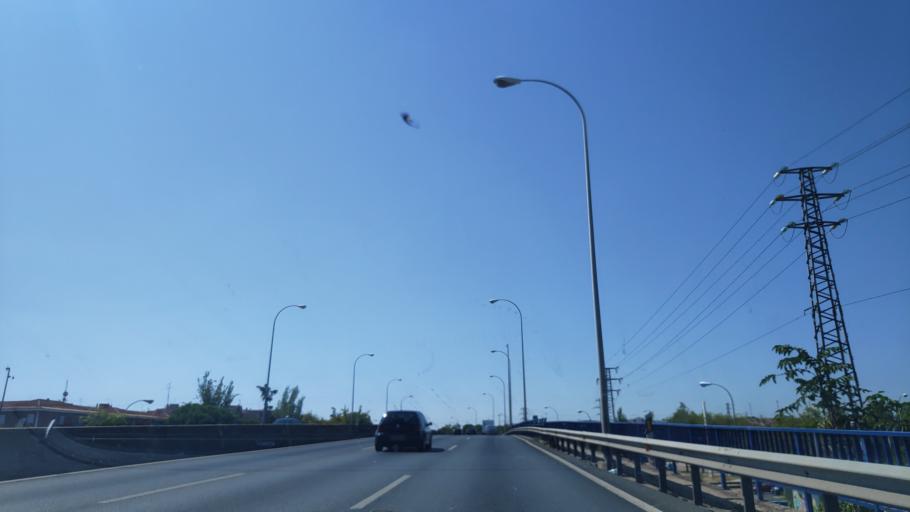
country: ES
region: Madrid
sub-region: Provincia de Madrid
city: Getafe
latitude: 40.3131
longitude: -3.7389
